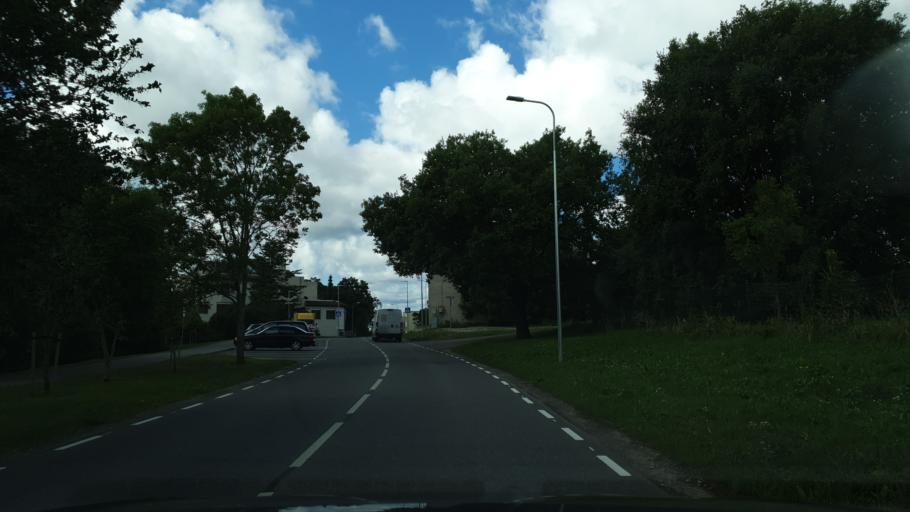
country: EE
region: Harju
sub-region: Viimsi vald
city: Viimsi
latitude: 59.5026
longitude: 24.8422
